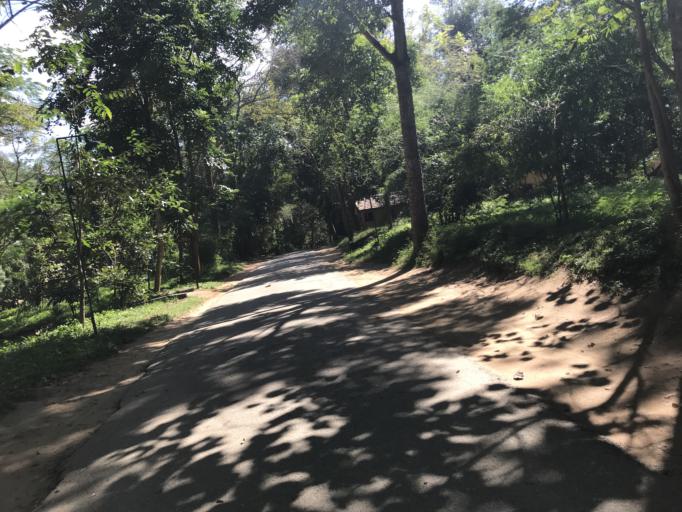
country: IN
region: Karnataka
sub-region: Mysore
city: Sargur
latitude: 11.9384
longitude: 76.2704
